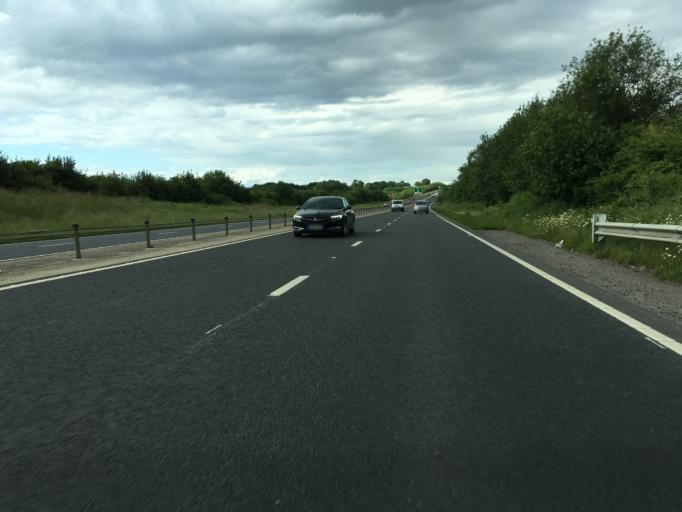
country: GB
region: England
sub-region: Central Bedfordshire
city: Leighton Buzzard
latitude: 51.9202
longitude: -0.6995
